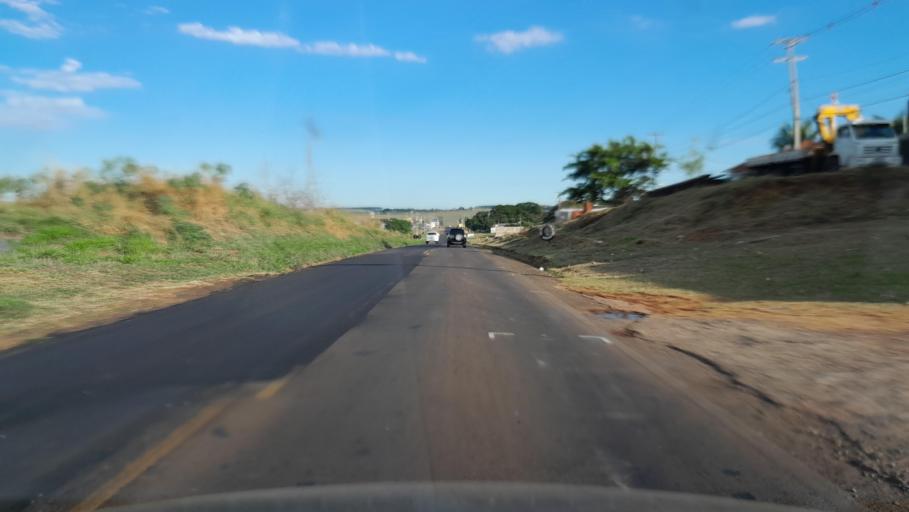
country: BR
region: Parana
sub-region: Umuarama
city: Umuarama
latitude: -23.7682
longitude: -53.2696
